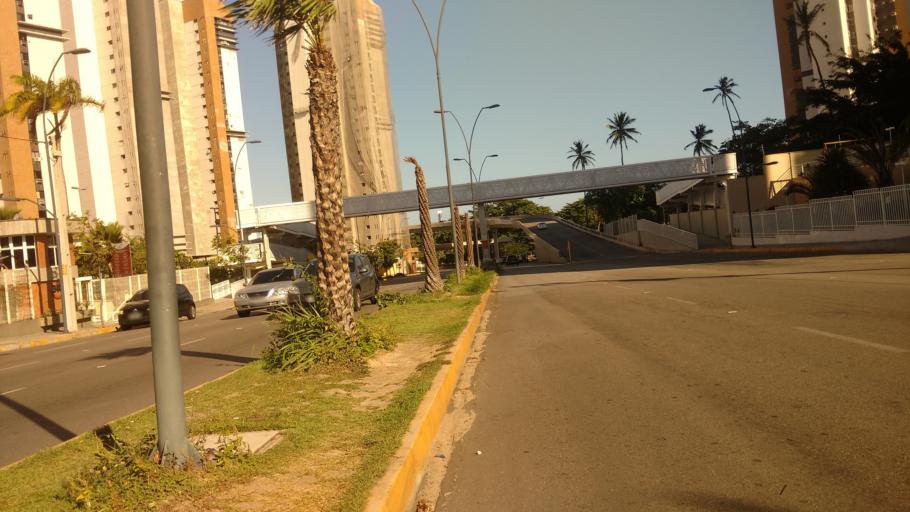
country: BR
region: Ceara
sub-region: Fortaleza
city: Fortaleza
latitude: -3.7486
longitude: -38.4922
